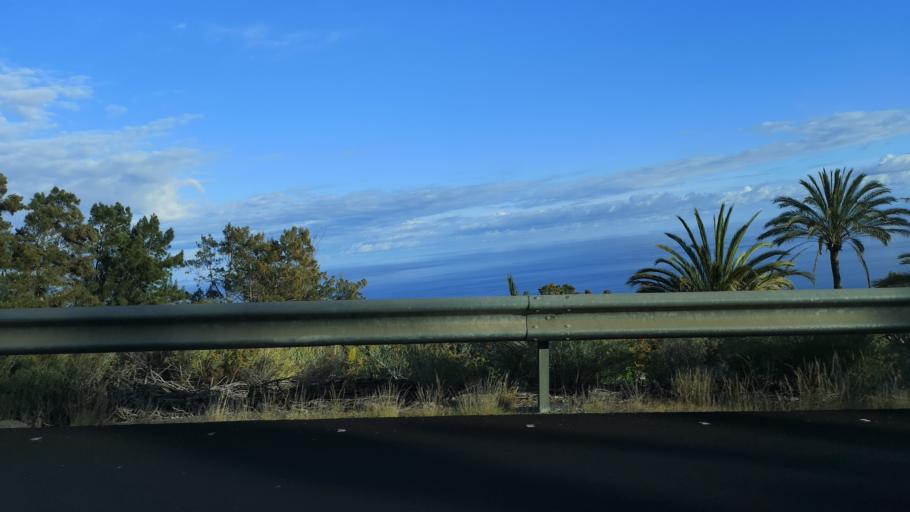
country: ES
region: Canary Islands
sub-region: Provincia de Santa Cruz de Tenerife
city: Alajero
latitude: 28.0428
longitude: -17.1940
